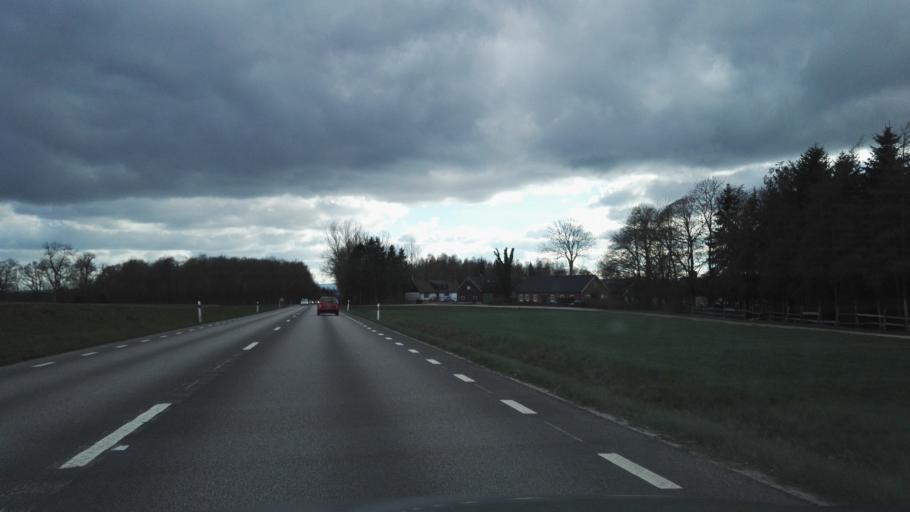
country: SE
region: Skane
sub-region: Sjobo Kommun
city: Sjoebo
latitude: 55.6613
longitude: 13.7079
